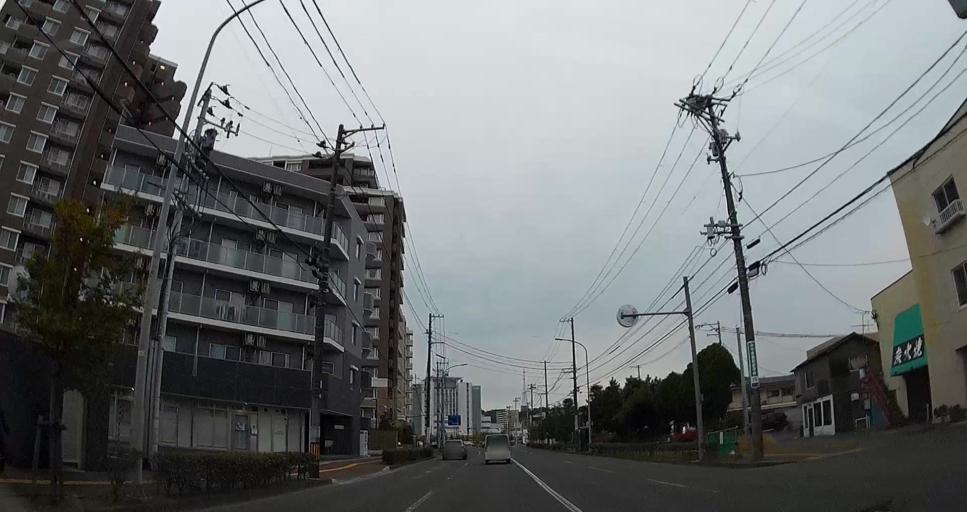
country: JP
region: Miyagi
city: Sendai
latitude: 38.2298
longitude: 140.8926
